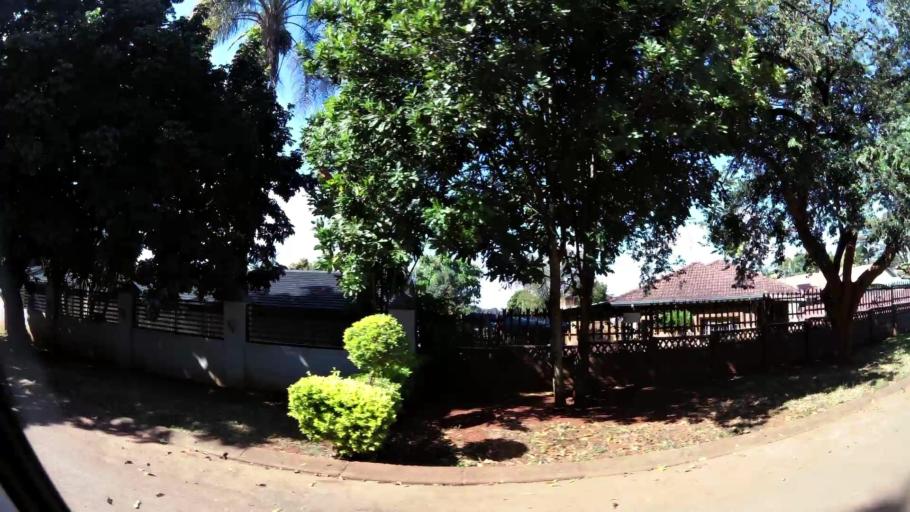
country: ZA
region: Limpopo
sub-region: Mopani District Municipality
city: Tzaneen
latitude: -23.8145
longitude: 30.1566
